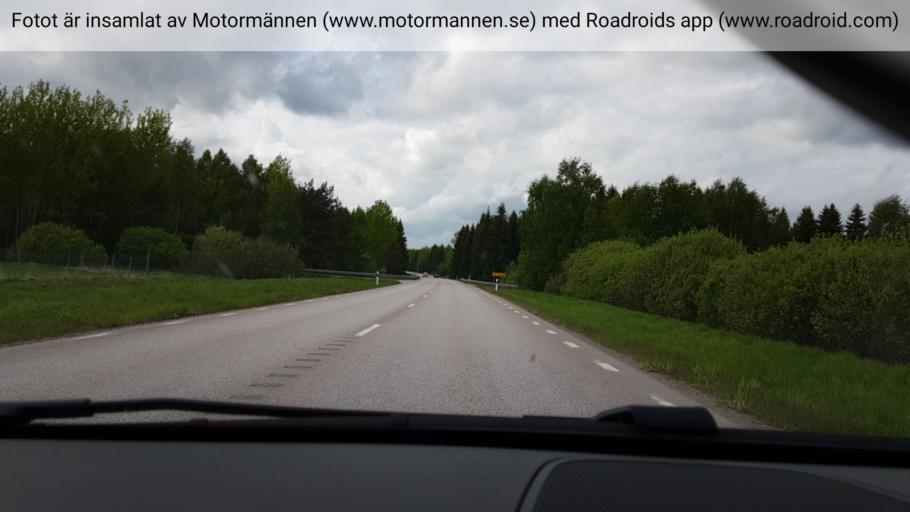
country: SE
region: Uppsala
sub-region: Tierps Kommun
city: Orbyhus
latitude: 60.2549
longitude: 17.6377
